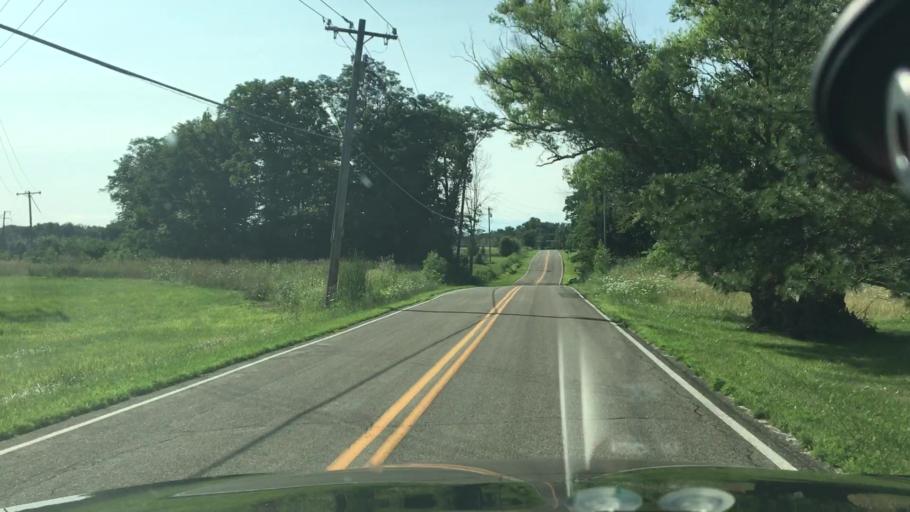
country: US
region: New York
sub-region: Erie County
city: North Collins
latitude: 42.6272
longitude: -78.9756
